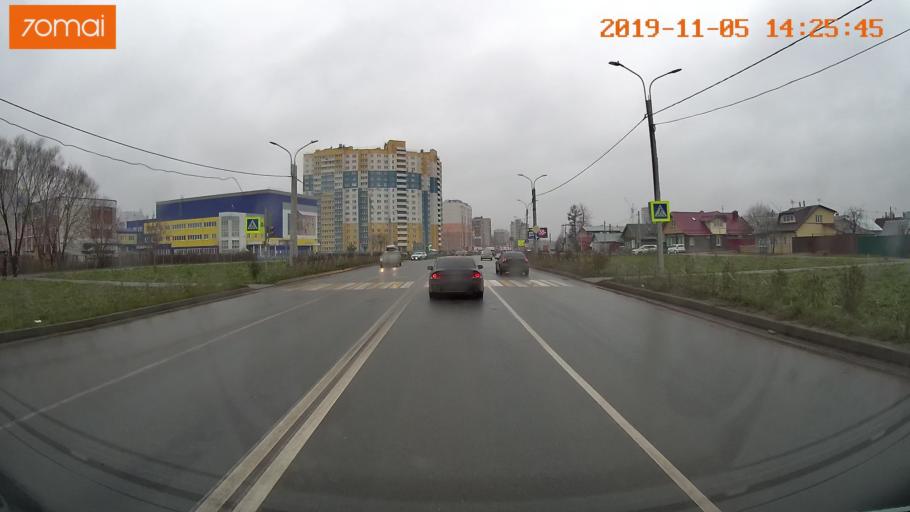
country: RU
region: Ivanovo
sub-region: Gorod Ivanovo
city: Ivanovo
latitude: 56.9714
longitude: 40.9925
